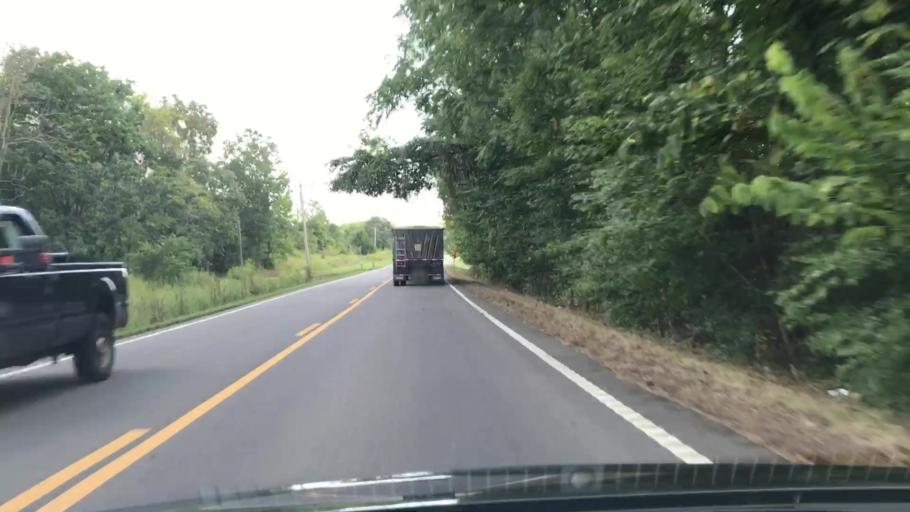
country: US
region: Tennessee
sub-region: Robertson County
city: Springfield
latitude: 36.6305
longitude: -86.9594
